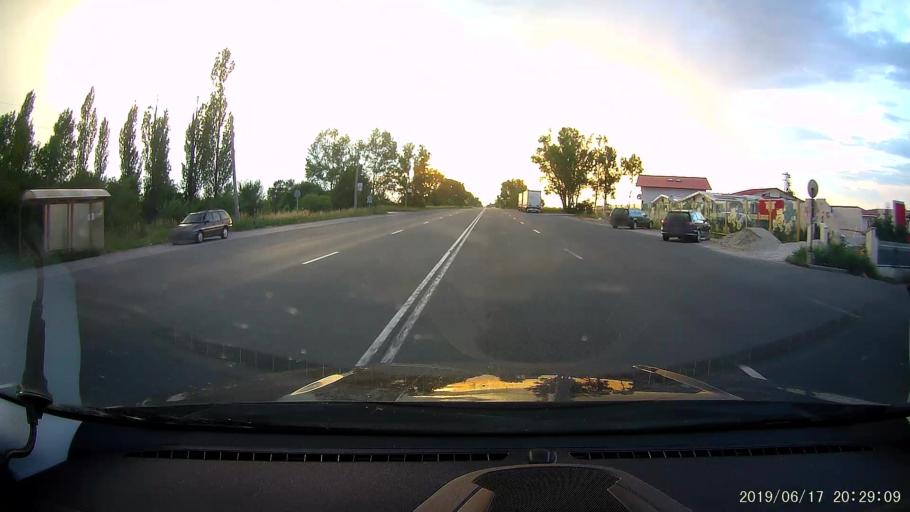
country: BG
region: Sofiya
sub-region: Obshtina Bozhurishte
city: Bozhurishte
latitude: 42.7837
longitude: 23.1668
